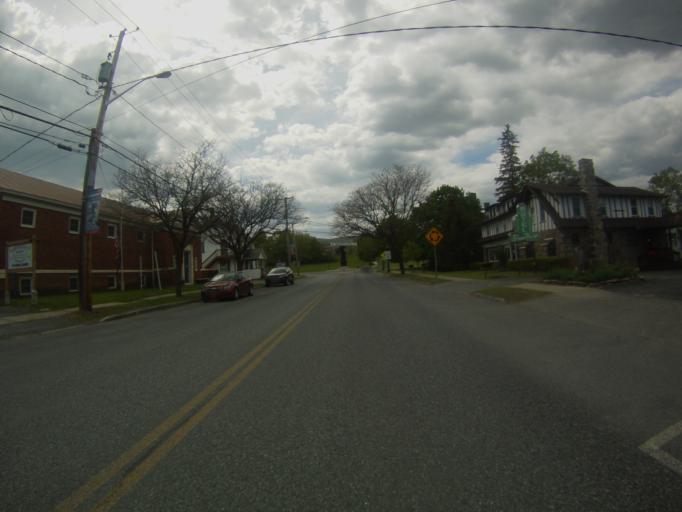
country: US
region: New York
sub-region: Essex County
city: Ticonderoga
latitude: 43.8484
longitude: -73.4335
